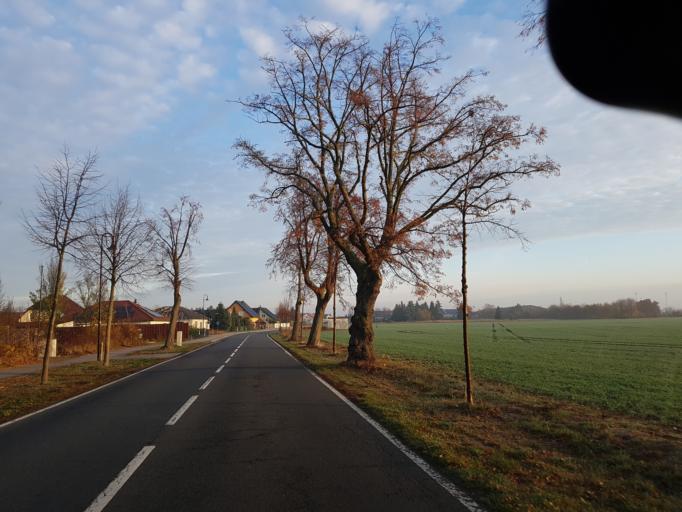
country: DE
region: Saxony-Anhalt
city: Elster
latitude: 51.8324
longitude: 12.8308
